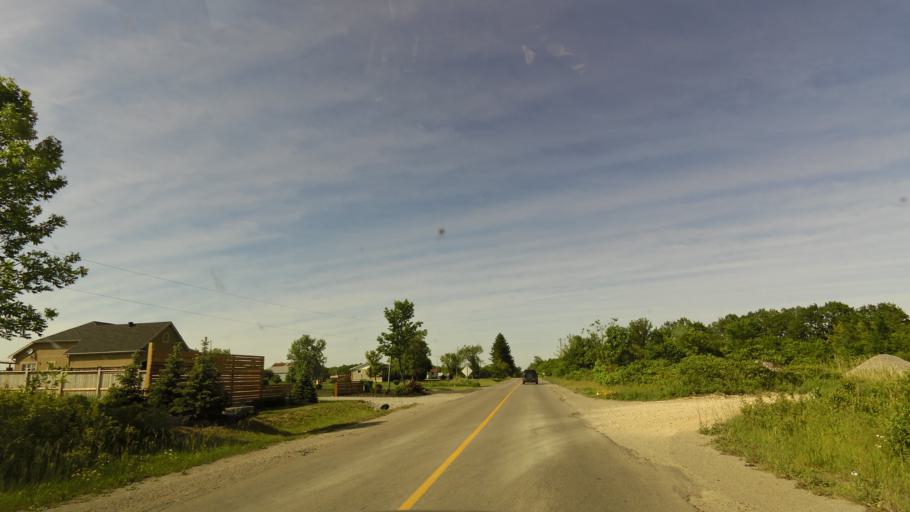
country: CA
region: Ontario
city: Ancaster
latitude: 43.0400
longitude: -80.0359
